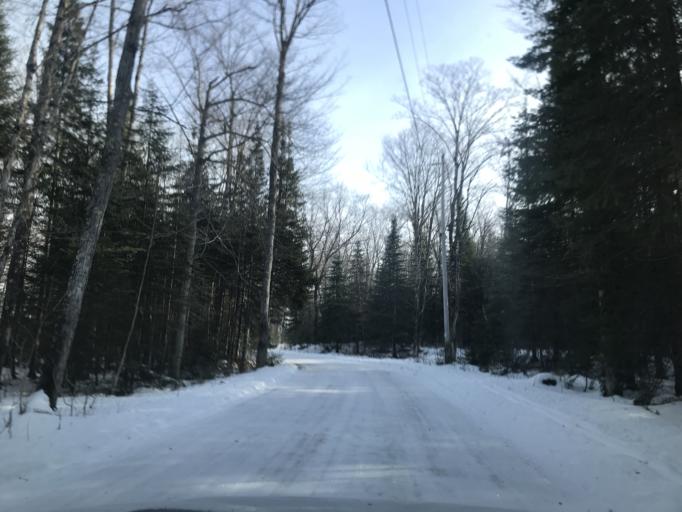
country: US
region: Wisconsin
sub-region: Door County
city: Sturgeon Bay
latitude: 45.1554
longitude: -87.0448
